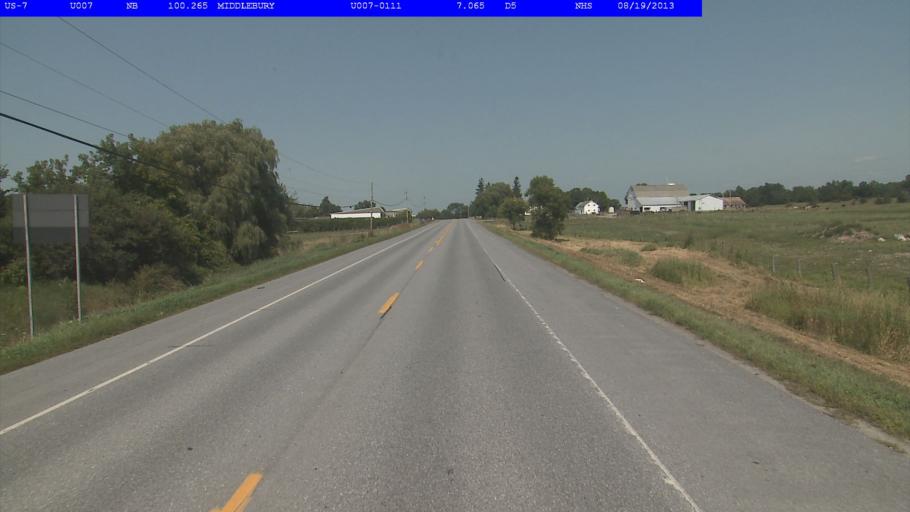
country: US
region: Vermont
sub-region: Addison County
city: Middlebury (village)
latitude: 44.0411
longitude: -73.1620
